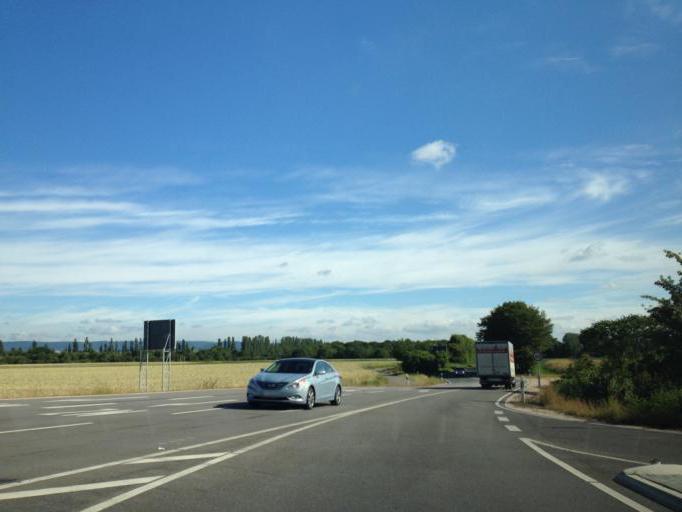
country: DE
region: Hesse
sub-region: Regierungsbezirk Darmstadt
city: Hochheim am Main
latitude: 50.0451
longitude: 8.3003
